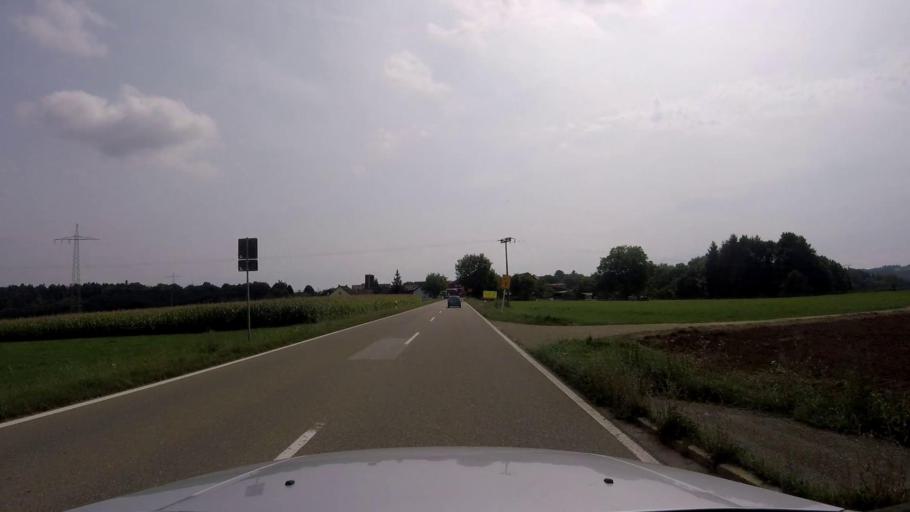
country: DE
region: Baden-Wuerttemberg
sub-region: Regierungsbezirk Stuttgart
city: Spraitbach
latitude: 48.8999
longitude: 9.7555
